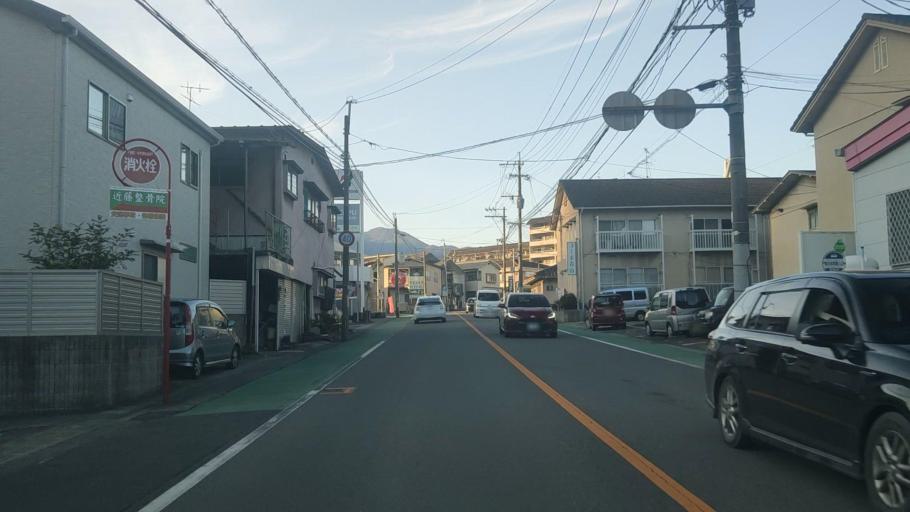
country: JP
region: Oita
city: Beppu
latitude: 33.2772
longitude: 131.4904
